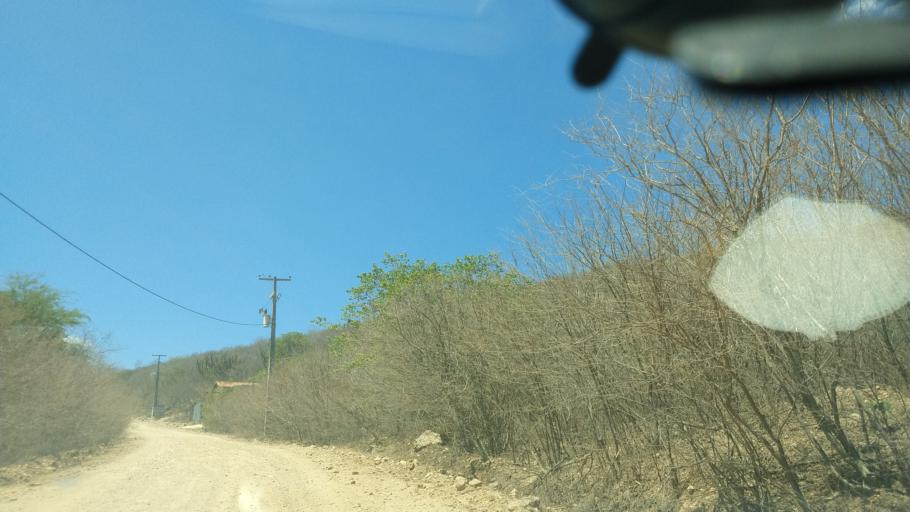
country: BR
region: Rio Grande do Norte
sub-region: Cerro Cora
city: Cerro Cora
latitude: -6.0109
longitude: -36.3182
